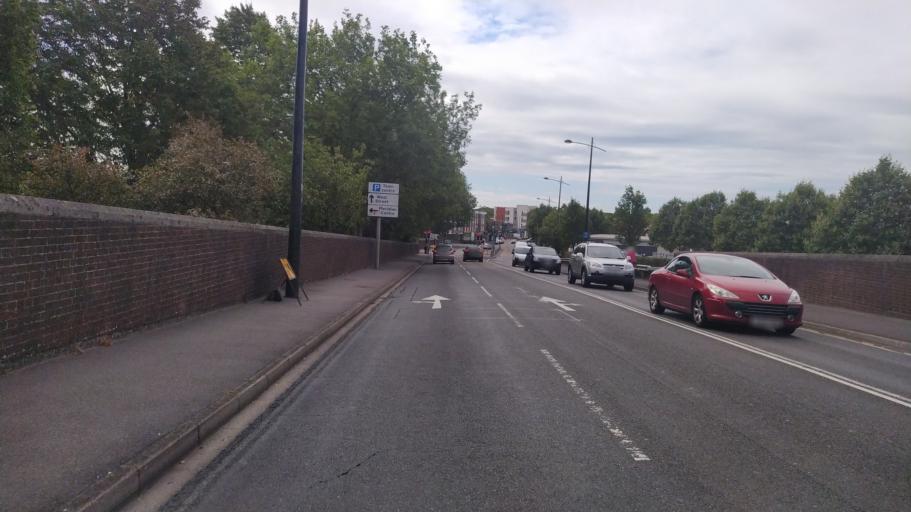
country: GB
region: England
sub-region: Hampshire
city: Havant
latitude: 50.8542
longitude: -0.9853
